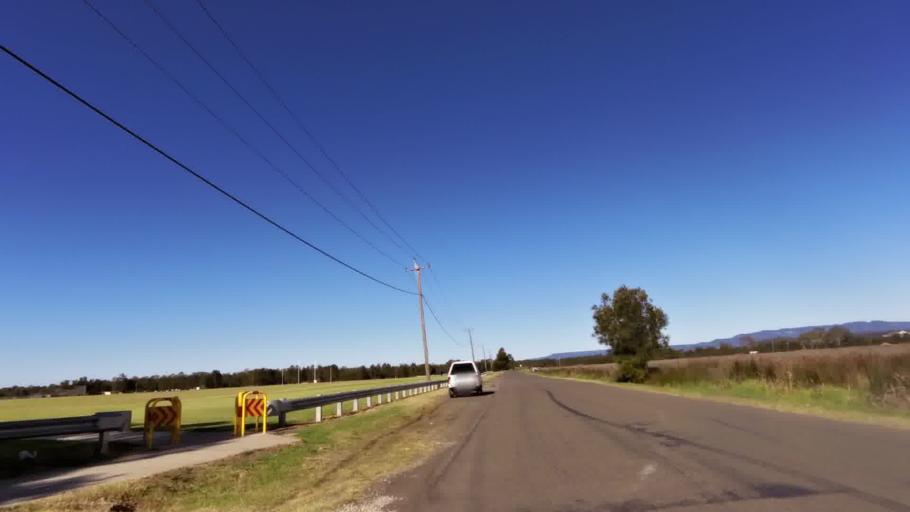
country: AU
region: New South Wales
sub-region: Wollongong
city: Berkeley
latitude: -34.4796
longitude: 150.8336
